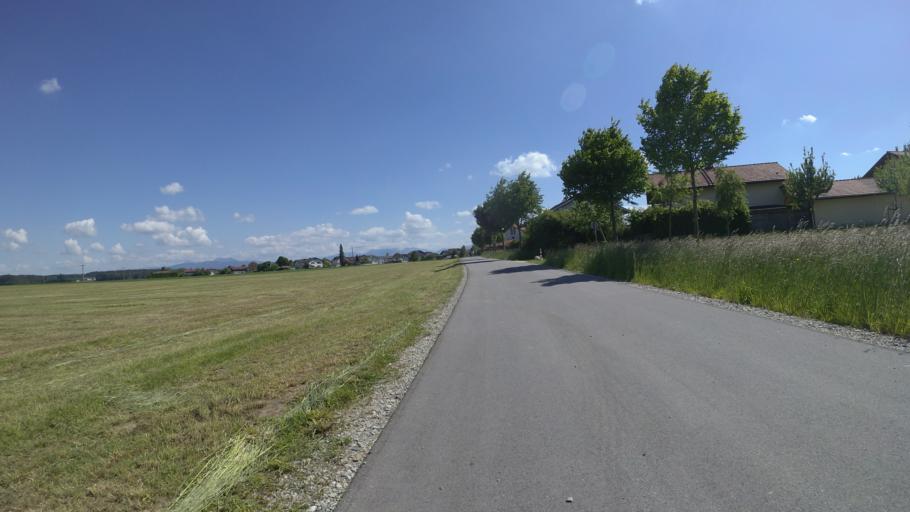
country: DE
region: Bavaria
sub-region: Upper Bavaria
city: Traunreut
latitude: 47.9444
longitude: 12.6053
